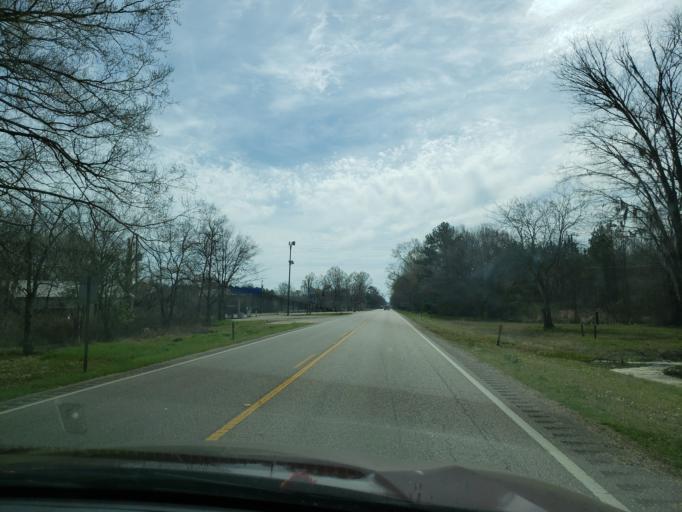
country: US
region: Alabama
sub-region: Dallas County
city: Selma
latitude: 32.4658
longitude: -87.0939
